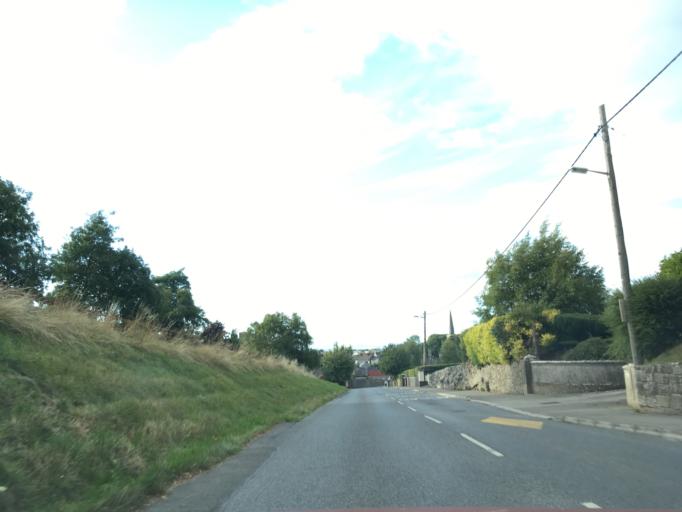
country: IE
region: Munster
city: Cashel
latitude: 52.5117
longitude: -7.8858
